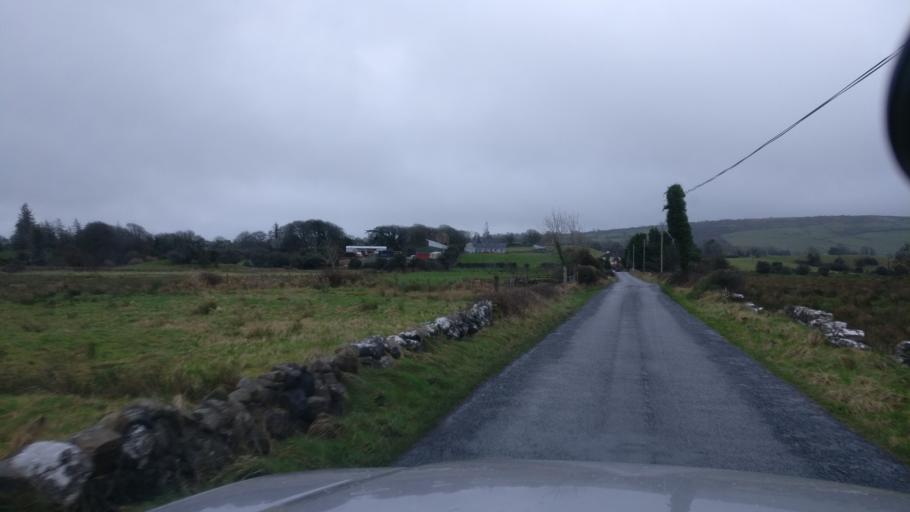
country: IE
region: Connaught
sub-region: County Galway
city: Loughrea
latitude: 53.1831
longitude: -8.6571
